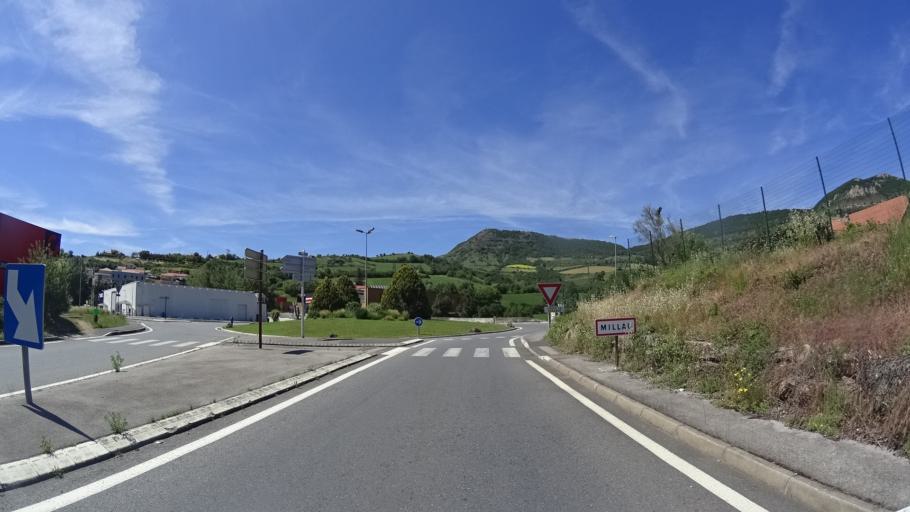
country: FR
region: Midi-Pyrenees
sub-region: Departement de l'Aveyron
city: Millau
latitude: 44.1181
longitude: 3.0707
